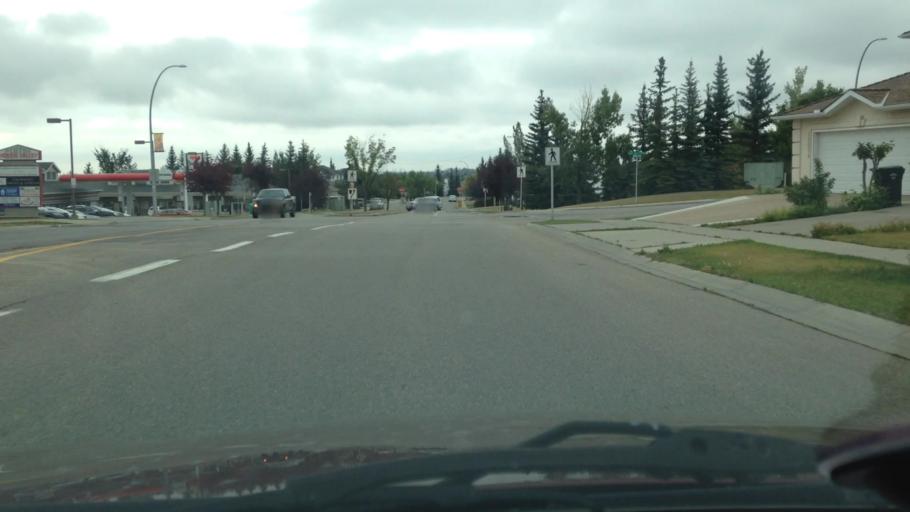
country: CA
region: Alberta
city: Calgary
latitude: 51.1471
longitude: -114.1077
